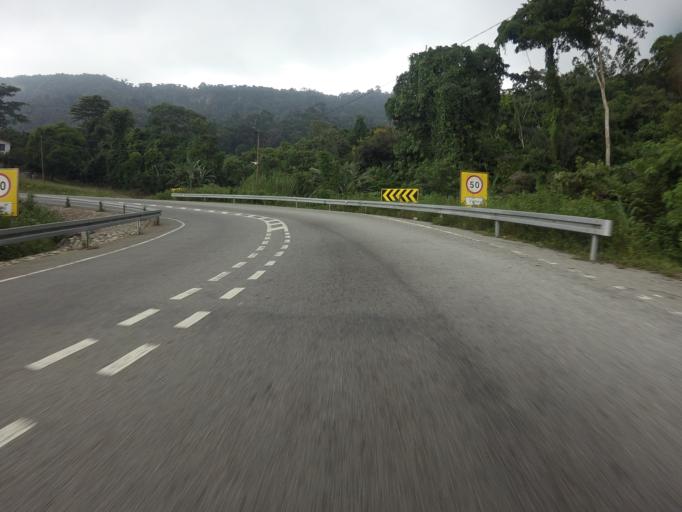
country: GH
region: Volta
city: Kpandu
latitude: 6.8198
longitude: 0.4261
